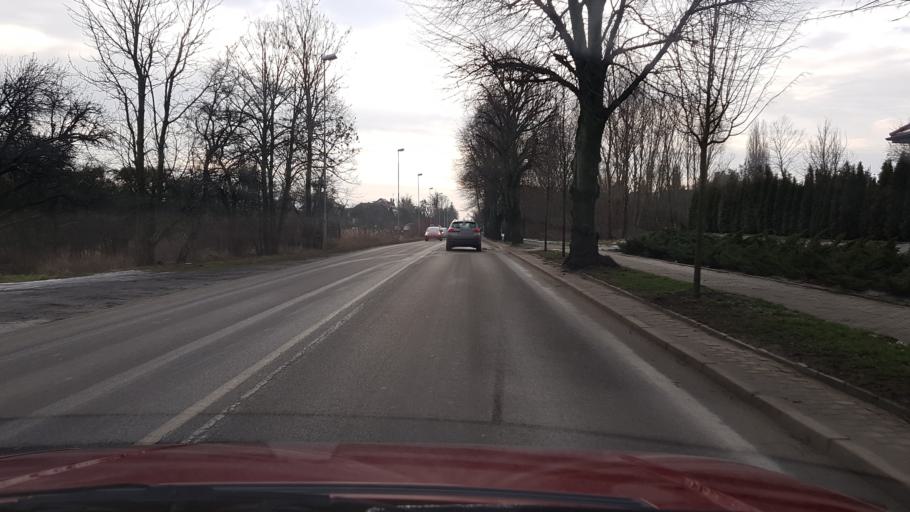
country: PL
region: West Pomeranian Voivodeship
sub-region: Szczecin
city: Szczecin
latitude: 53.4852
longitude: 14.5862
